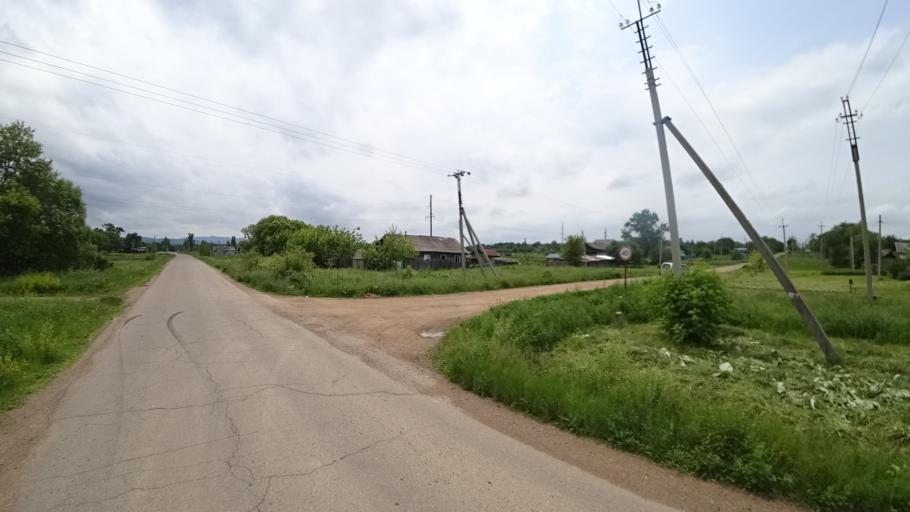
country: RU
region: Primorskiy
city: Novosysoyevka
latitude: 44.2343
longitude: 133.3705
